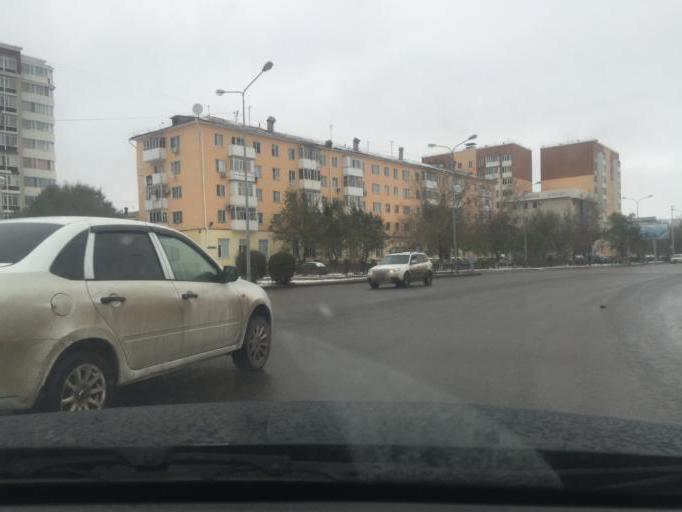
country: KZ
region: Astana Qalasy
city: Astana
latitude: 51.1916
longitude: 71.4068
